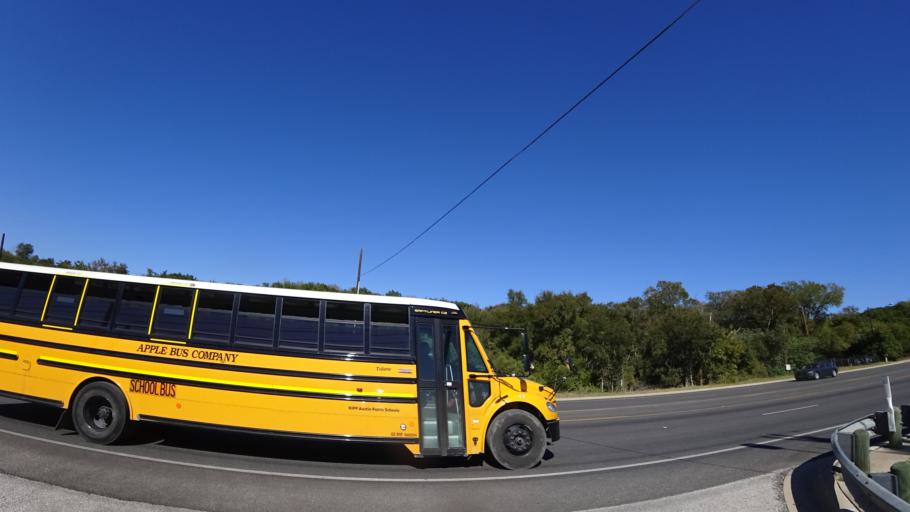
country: US
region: Texas
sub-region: Travis County
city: Hornsby Bend
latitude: 30.2784
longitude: -97.6420
